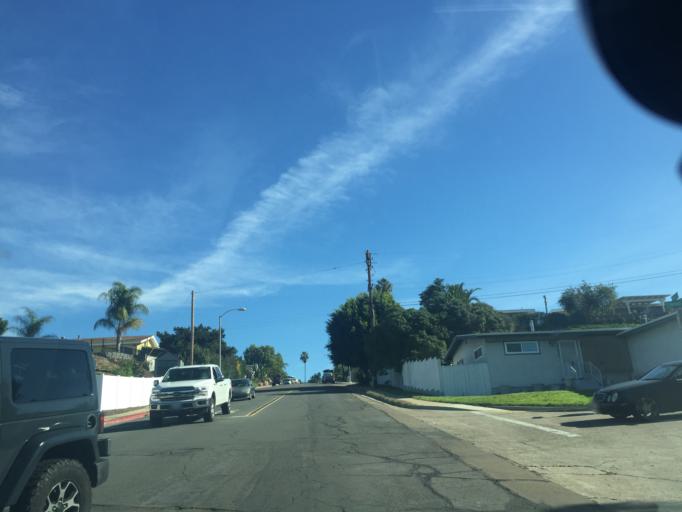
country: US
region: California
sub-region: San Diego County
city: La Mesa
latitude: 32.7849
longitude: -117.0941
